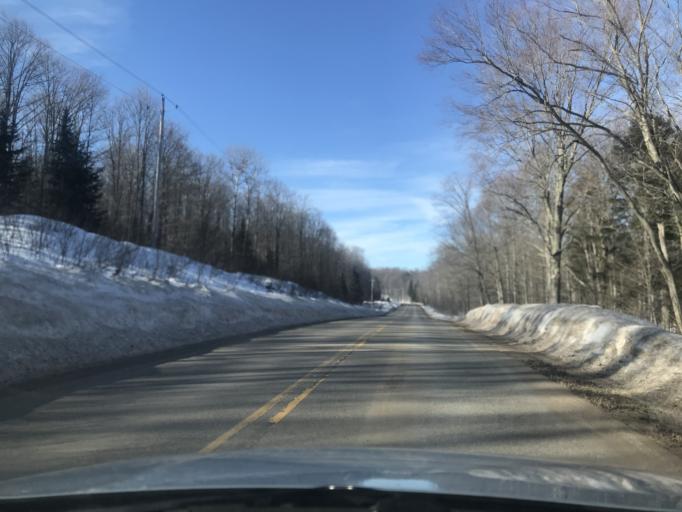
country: US
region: Michigan
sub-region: Dickinson County
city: Kingsford
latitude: 45.4193
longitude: -88.4101
